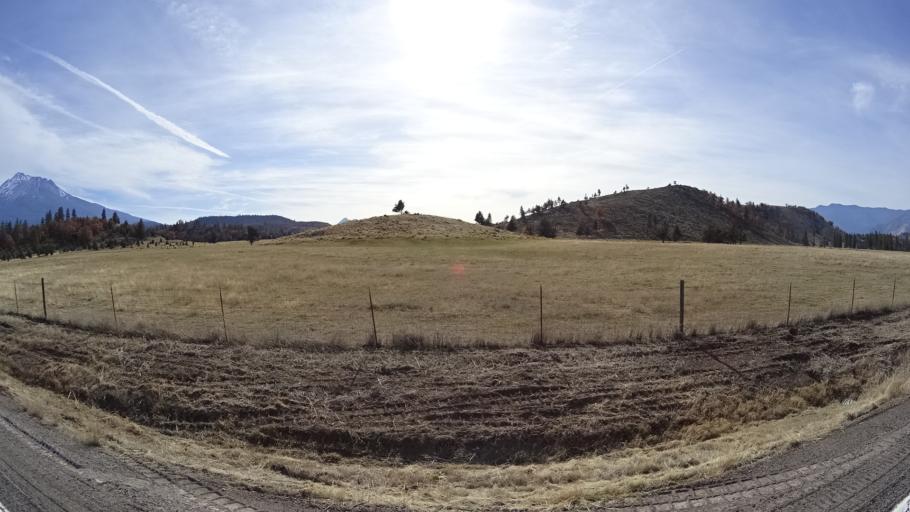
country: US
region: California
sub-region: Siskiyou County
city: Weed
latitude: 41.4941
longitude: -122.3896
